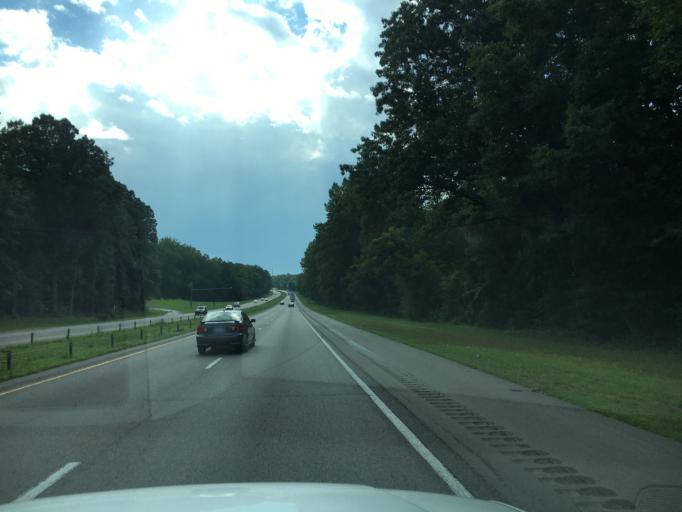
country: US
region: North Carolina
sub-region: Alexander County
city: Stony Point
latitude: 35.7608
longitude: -81.0312
